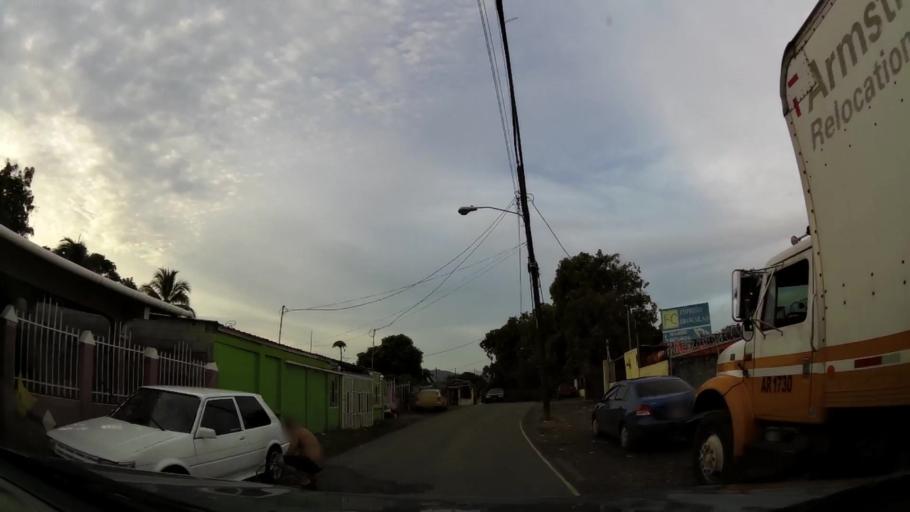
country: PA
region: Panama
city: Tocumen
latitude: 9.0884
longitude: -79.3895
